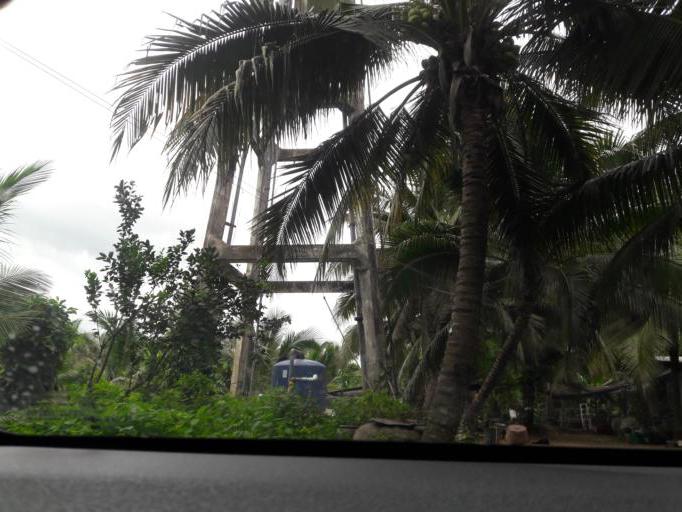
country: TH
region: Ratchaburi
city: Damnoen Saduak
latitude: 13.5664
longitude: 99.9975
